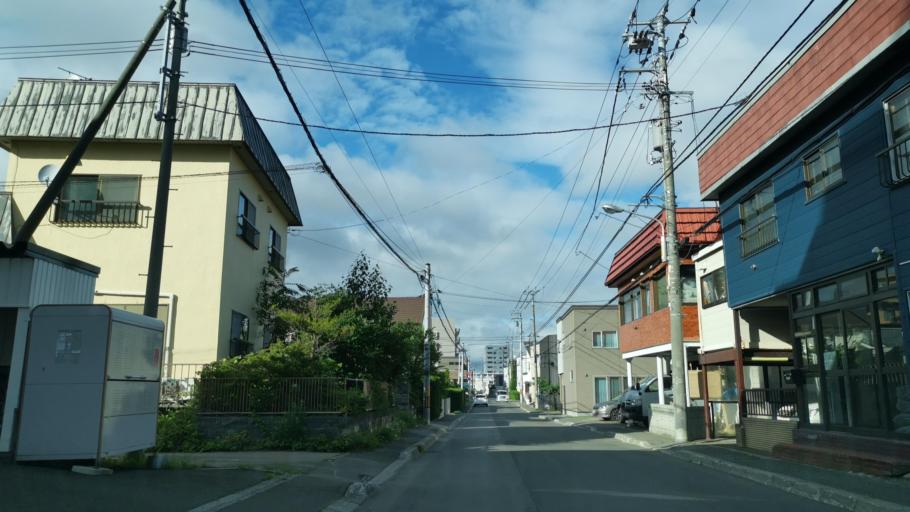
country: JP
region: Hokkaido
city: Sapporo
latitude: 43.0677
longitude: 141.3001
